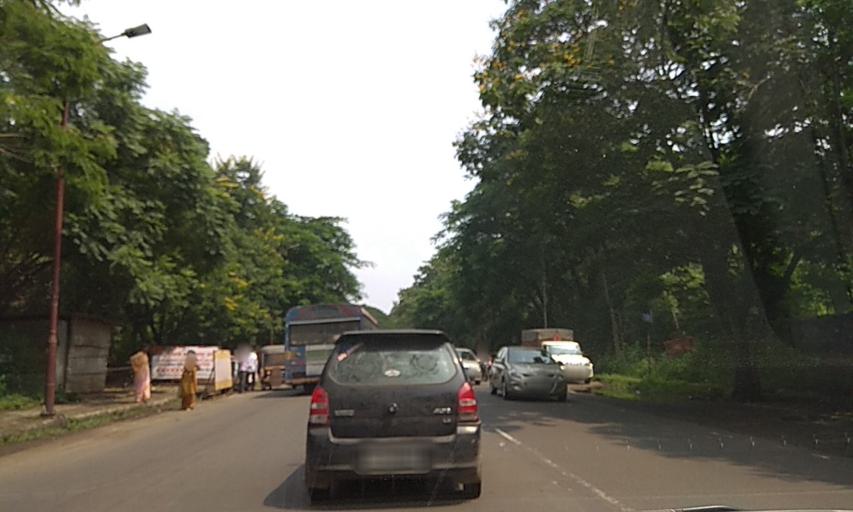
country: IN
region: Maharashtra
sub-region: Pune Division
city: Shivaji Nagar
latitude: 18.5399
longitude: 73.8164
